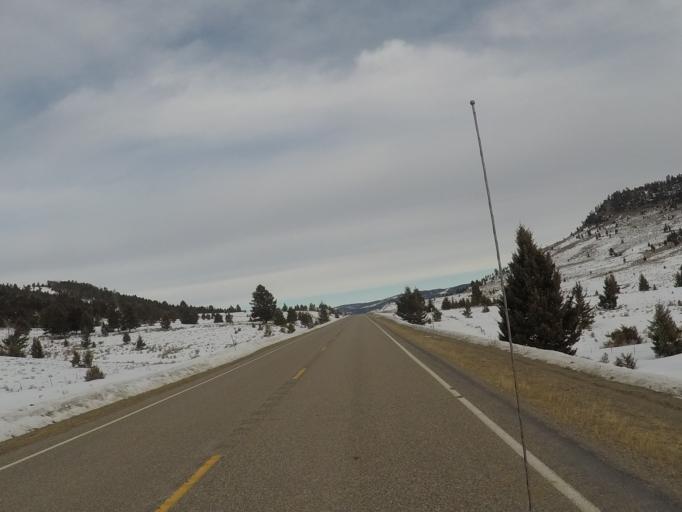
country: US
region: Montana
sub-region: Meagher County
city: White Sulphur Springs
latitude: 46.6410
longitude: -110.8616
